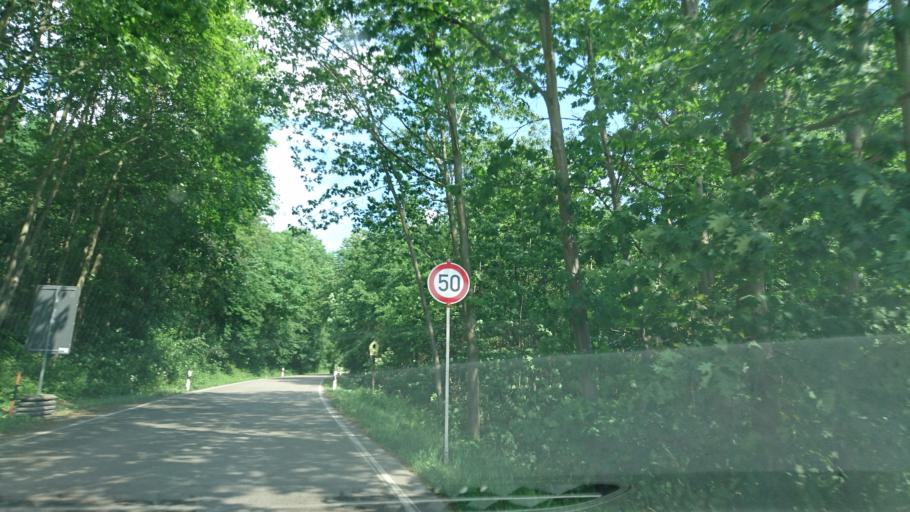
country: DE
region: Saxony
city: Struppen
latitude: 50.9197
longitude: 13.9761
